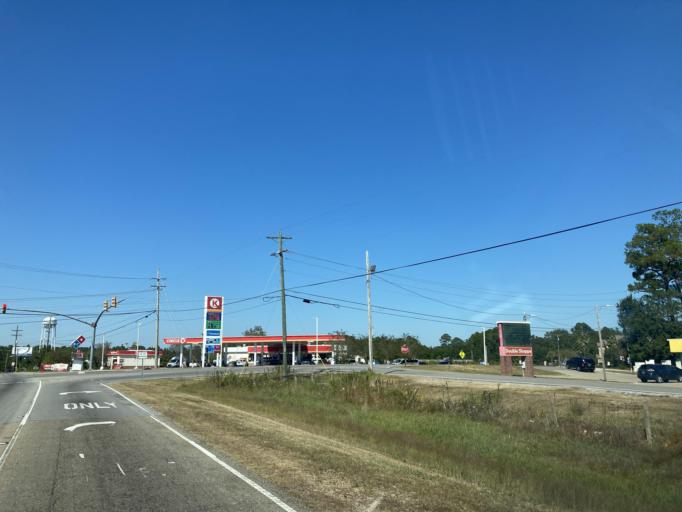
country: US
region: Mississippi
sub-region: Jackson County
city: Gulf Hills
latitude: 30.4571
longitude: -88.8432
